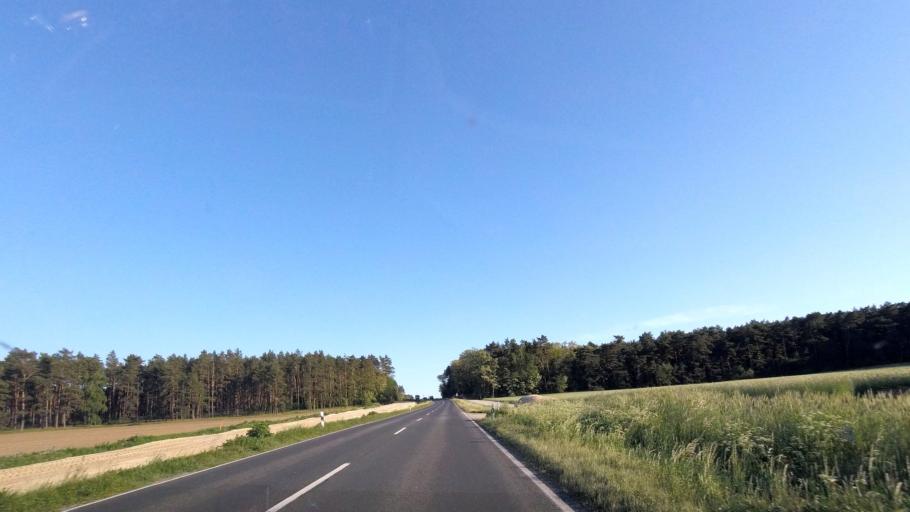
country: DE
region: Brandenburg
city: Brandenburg an der Havel
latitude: 52.3586
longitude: 12.5976
